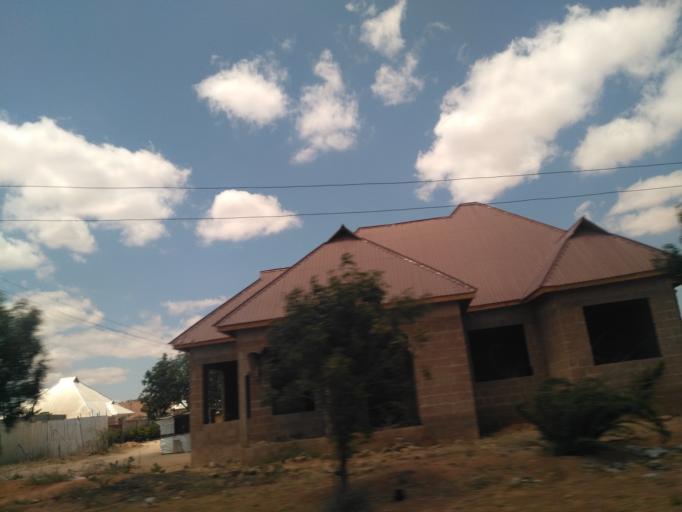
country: TZ
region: Dodoma
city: Kisasa
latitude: -6.1810
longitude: 35.7911
